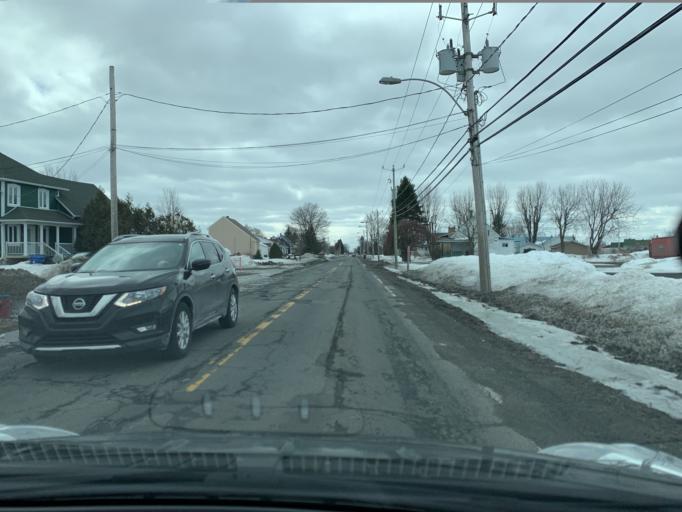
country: CA
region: Quebec
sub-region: Monteregie
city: Sainte-Julie
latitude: 45.6573
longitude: -73.2908
